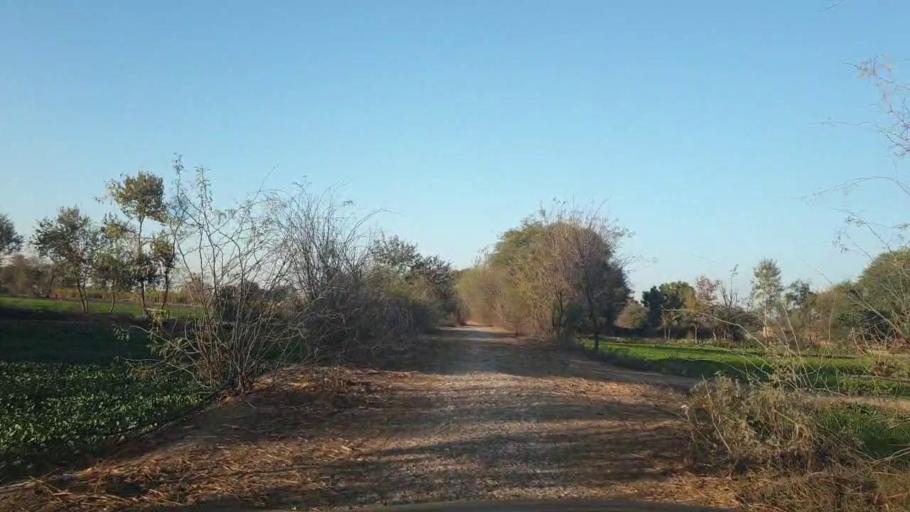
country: PK
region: Sindh
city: Mirpur Mathelo
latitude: 28.0079
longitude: 69.4612
